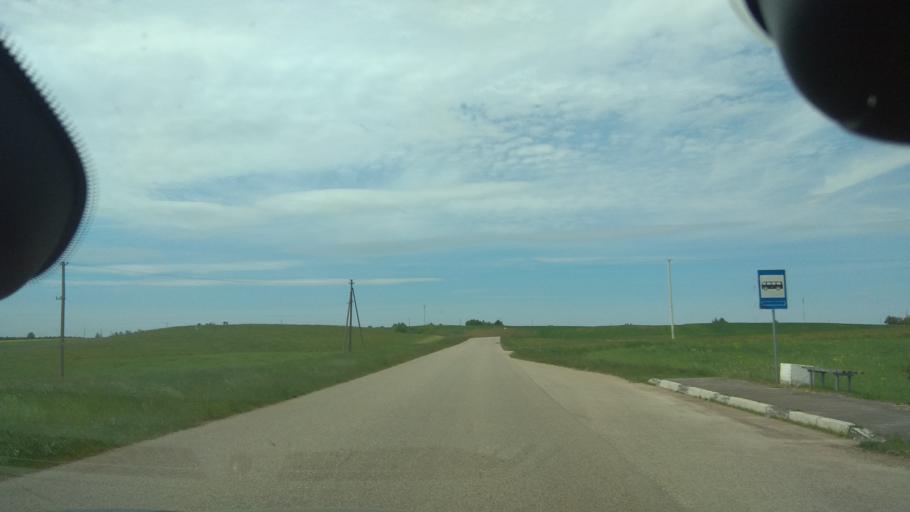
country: LT
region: Vilnius County
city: Ukmerge
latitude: 55.1611
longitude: 24.5409
